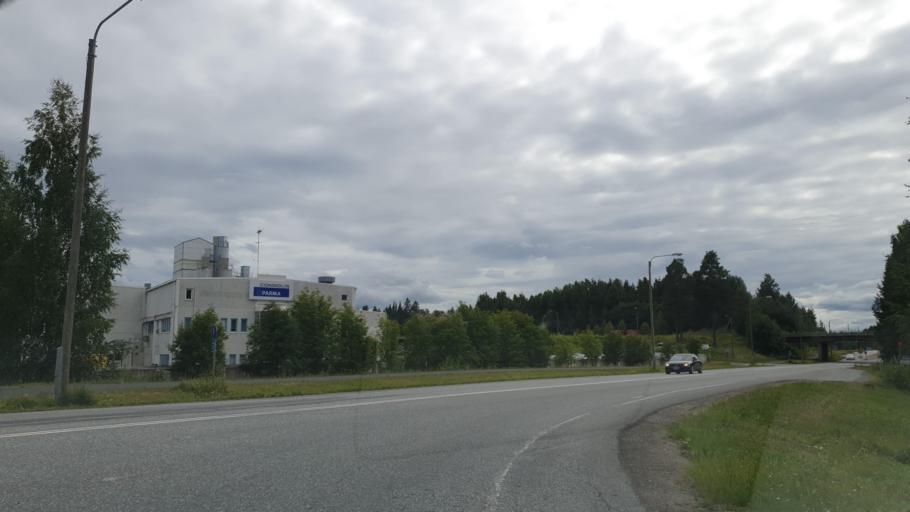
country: FI
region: Northern Savo
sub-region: Ylae-Savo
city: Iisalmi
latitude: 63.5245
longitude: 27.2469
